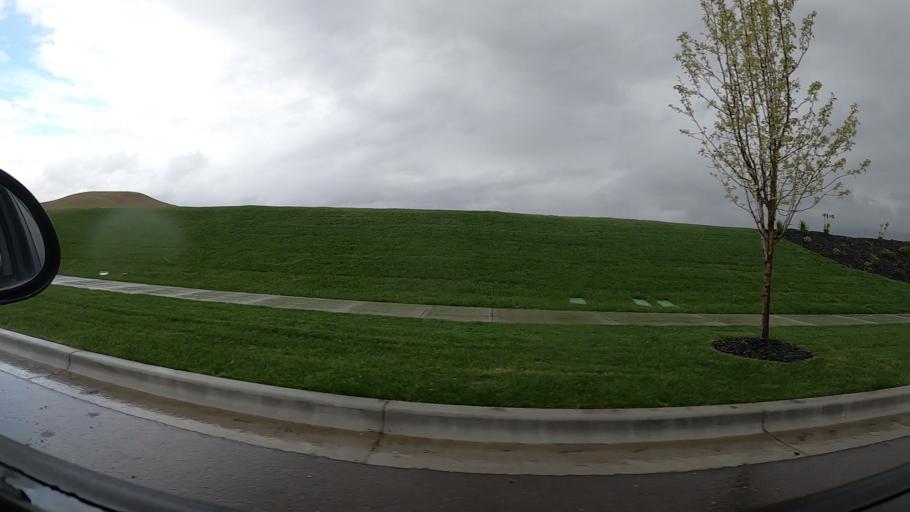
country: US
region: Idaho
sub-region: Ada County
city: Eagle
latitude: 43.7343
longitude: -116.2807
